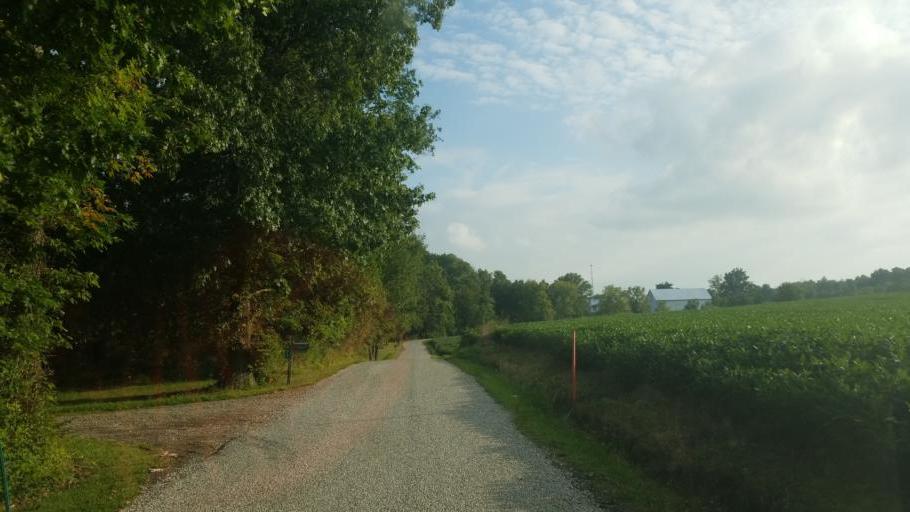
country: US
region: Ohio
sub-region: Wayne County
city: Wooster
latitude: 40.8111
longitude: -82.0421
